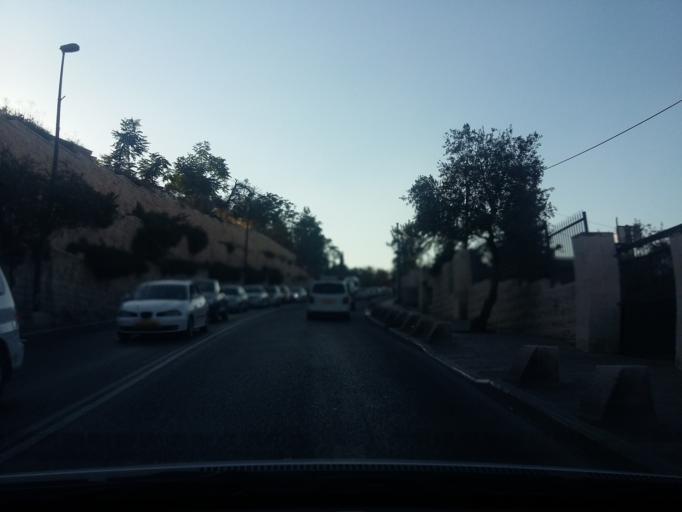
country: PS
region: West Bank
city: East Jerusalem
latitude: 31.7826
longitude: 35.2384
